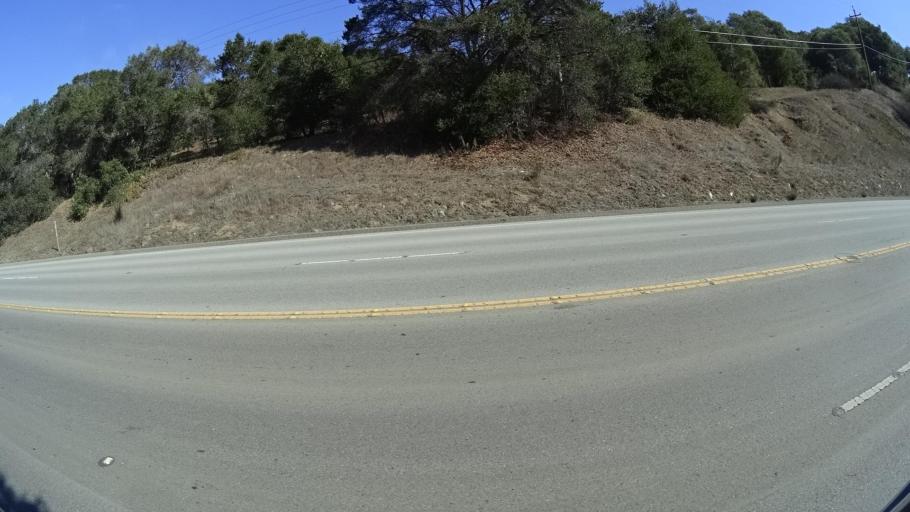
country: US
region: California
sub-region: San Benito County
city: Aromas
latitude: 36.8847
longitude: -121.6632
